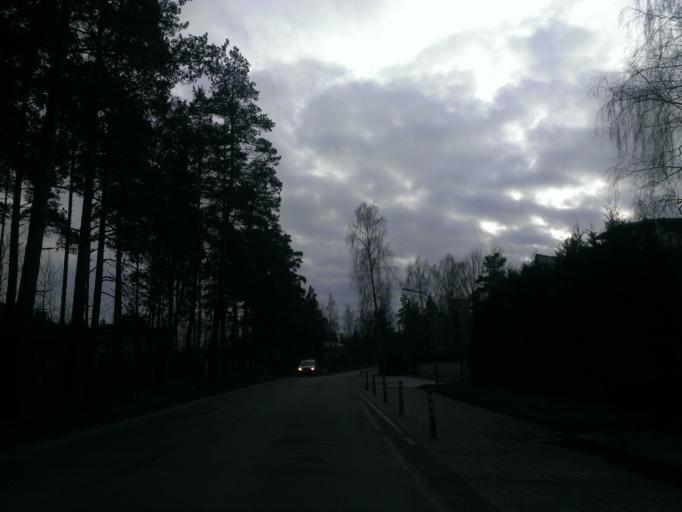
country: LV
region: Riga
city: Bergi
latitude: 56.9983
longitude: 24.3346
